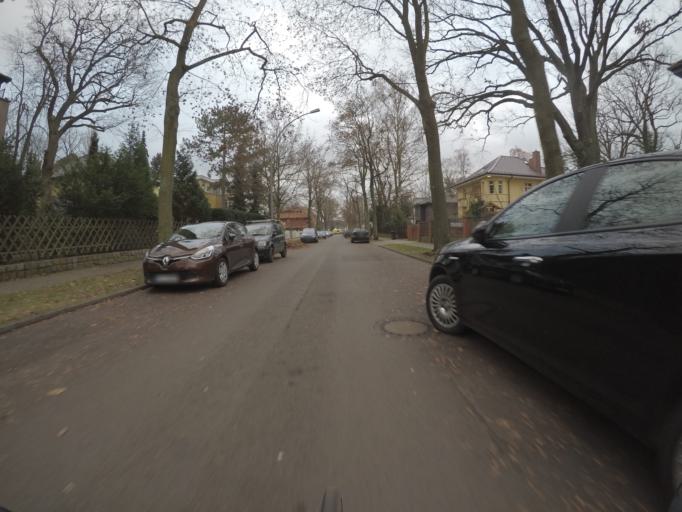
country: DE
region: Berlin
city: Grunau
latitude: 52.4155
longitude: 13.5899
